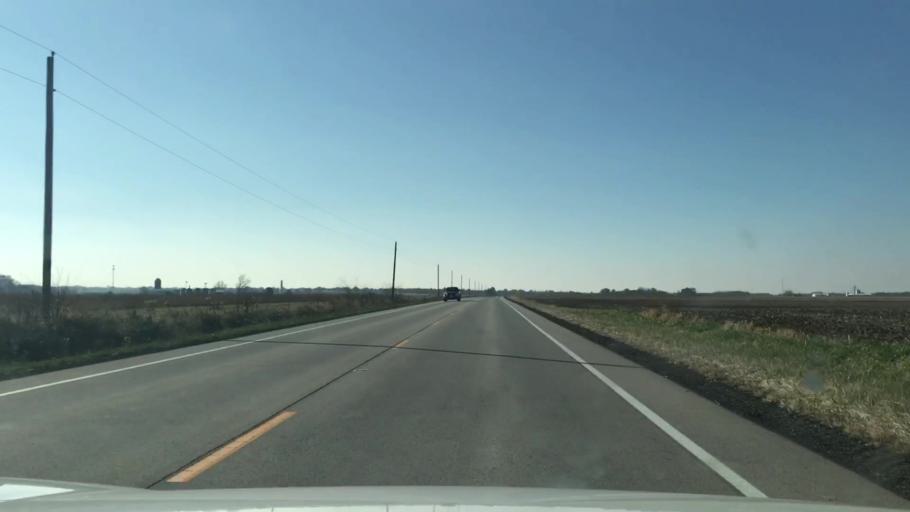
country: US
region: Illinois
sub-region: Washington County
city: Okawville
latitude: 38.4426
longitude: -89.5109
